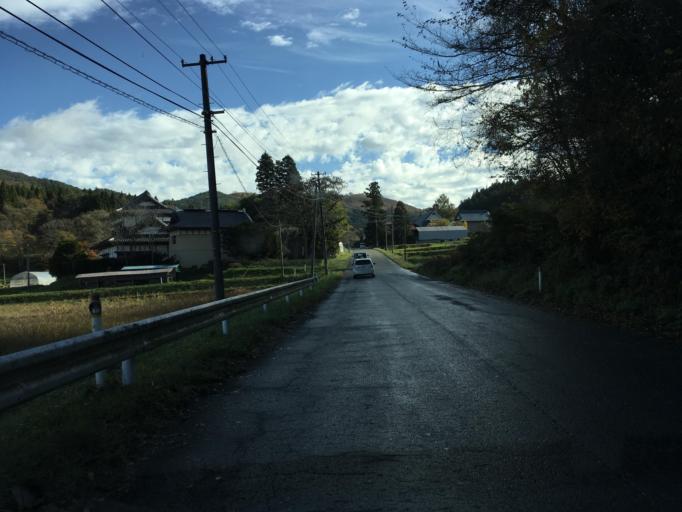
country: JP
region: Iwate
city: Ichinoseki
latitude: 38.8931
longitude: 141.4441
